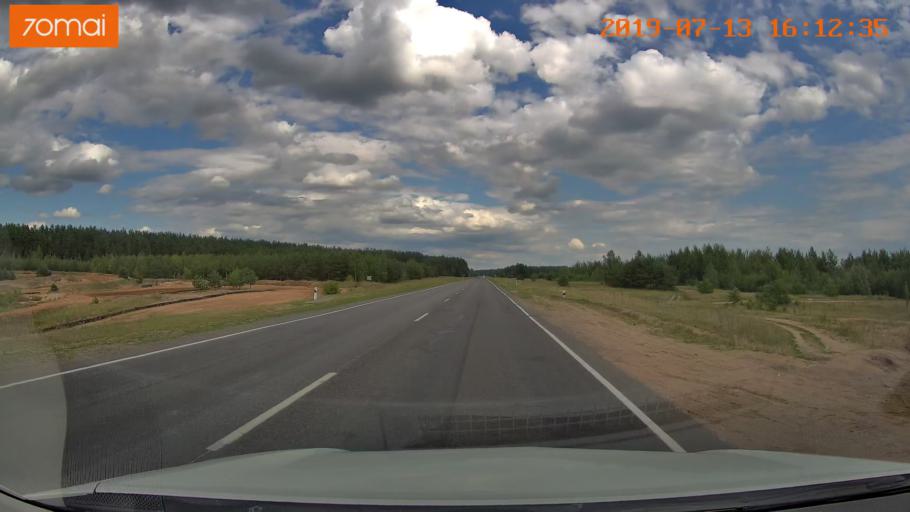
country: BY
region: Mogilev
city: Babruysk
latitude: 53.1664
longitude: 29.2836
